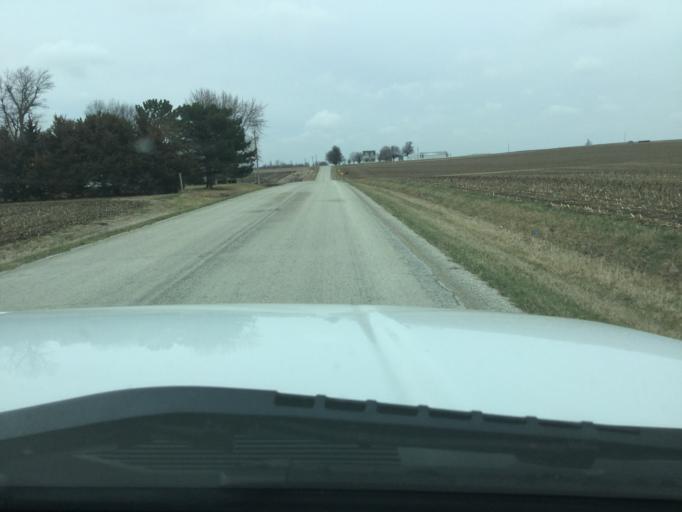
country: US
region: Kansas
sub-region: Nemaha County
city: Sabetha
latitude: 39.8457
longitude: -95.7142
